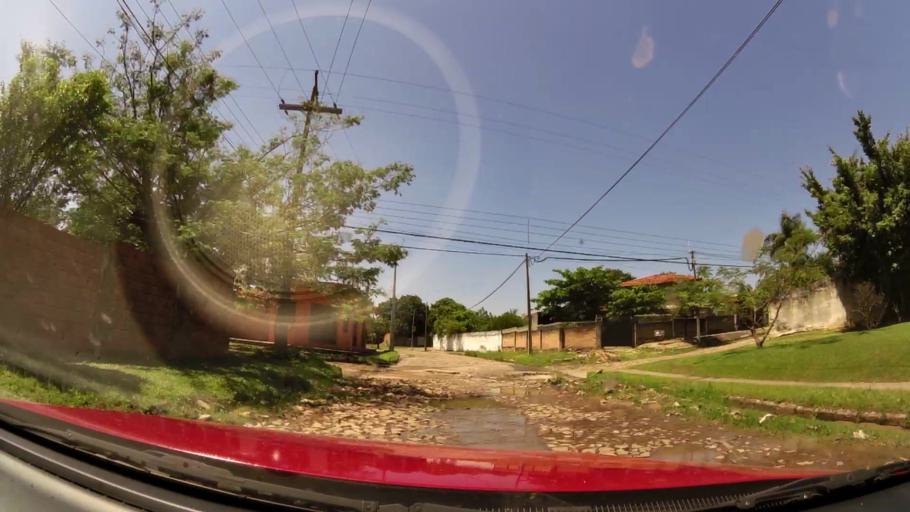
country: PY
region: Central
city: Colonia Mariano Roque Alonso
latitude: -25.2363
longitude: -57.5488
